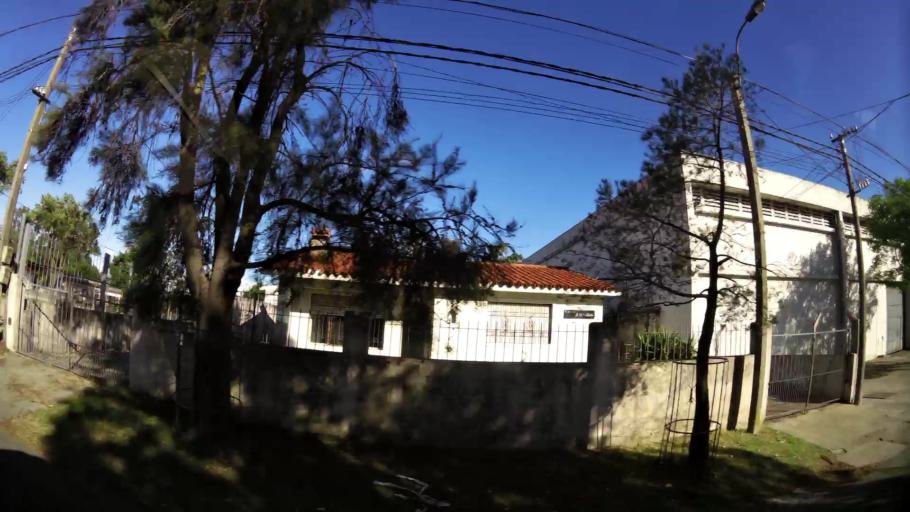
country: UY
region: Montevideo
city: Montevideo
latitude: -34.8459
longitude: -56.2337
